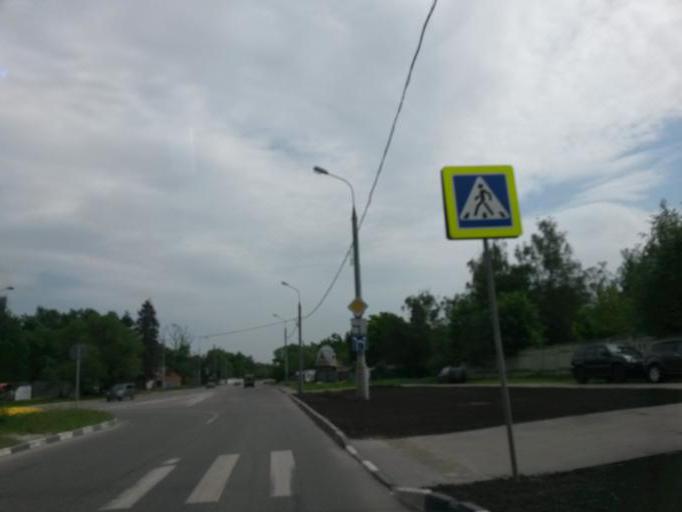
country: RU
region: Moskovskaya
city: Shcherbinka
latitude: 55.5407
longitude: 37.5573
